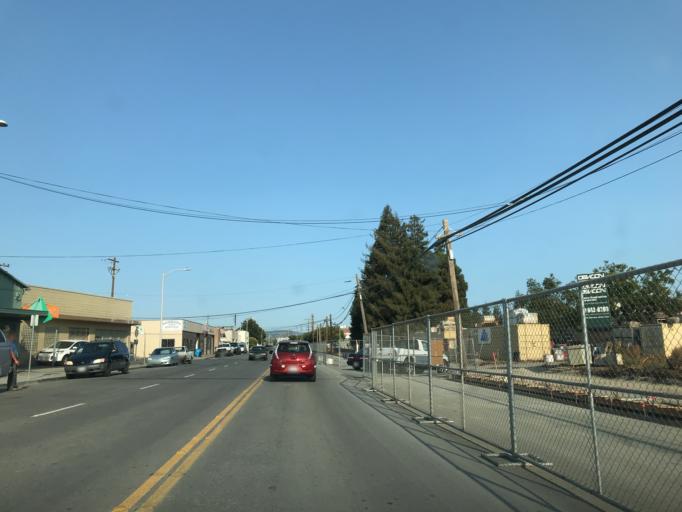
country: US
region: California
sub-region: San Mateo County
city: North Fair Oaks
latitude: 37.4838
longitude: -122.2058
